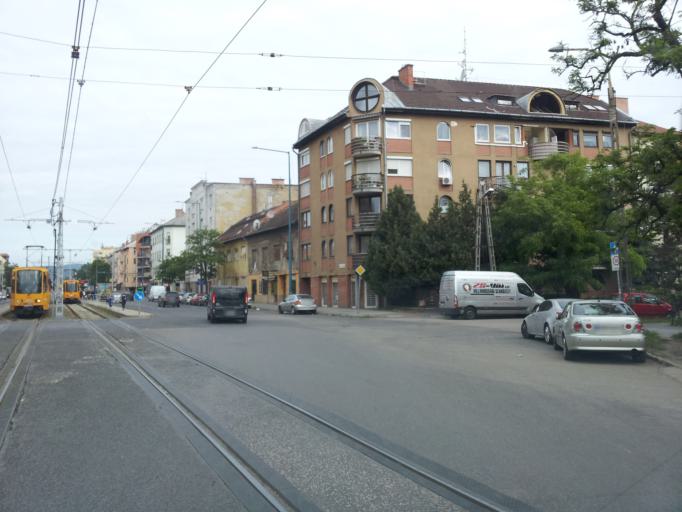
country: HU
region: Budapest
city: Budapest XIV. keruelet
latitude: 47.5219
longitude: 19.1039
